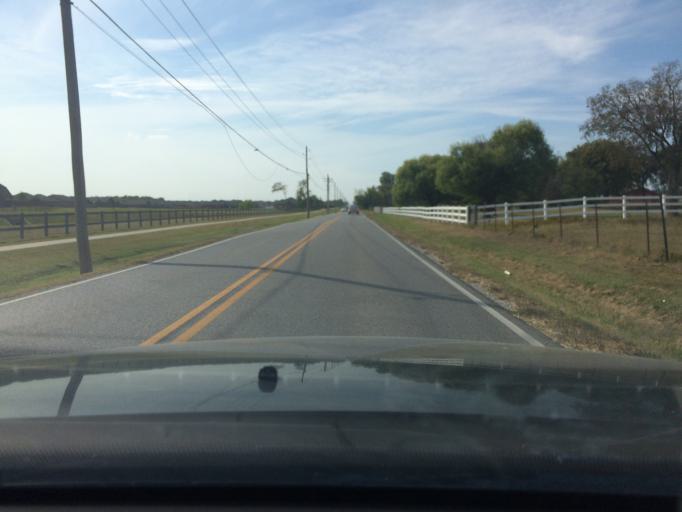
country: US
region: Oklahoma
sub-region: Tulsa County
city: Broken Arrow
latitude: 36.1045
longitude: -95.7683
